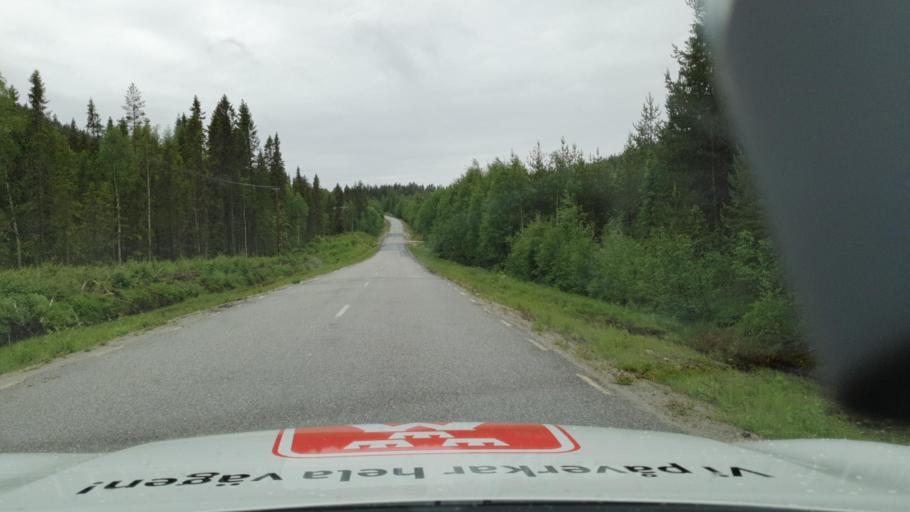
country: SE
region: Vaesterbotten
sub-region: Asele Kommun
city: Asele
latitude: 63.9755
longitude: 17.1380
